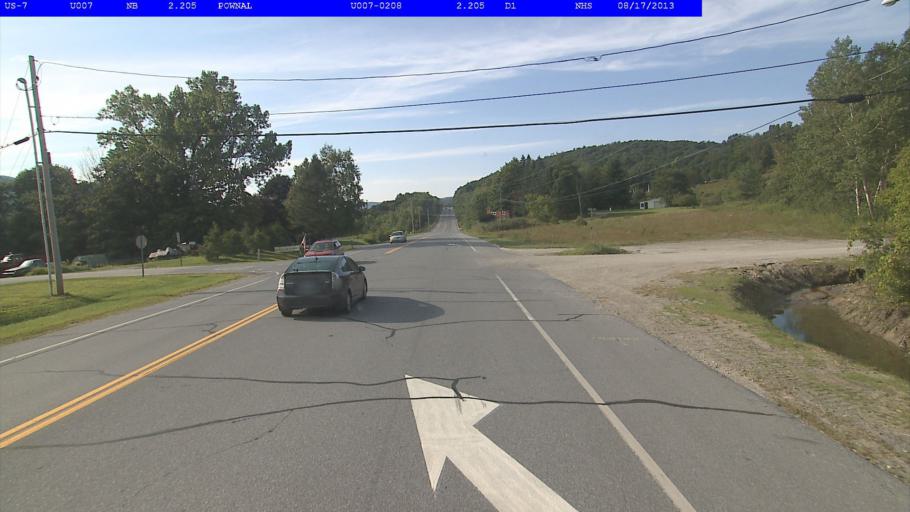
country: US
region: Massachusetts
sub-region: Berkshire County
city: Williamstown
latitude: 42.7680
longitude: -73.2345
